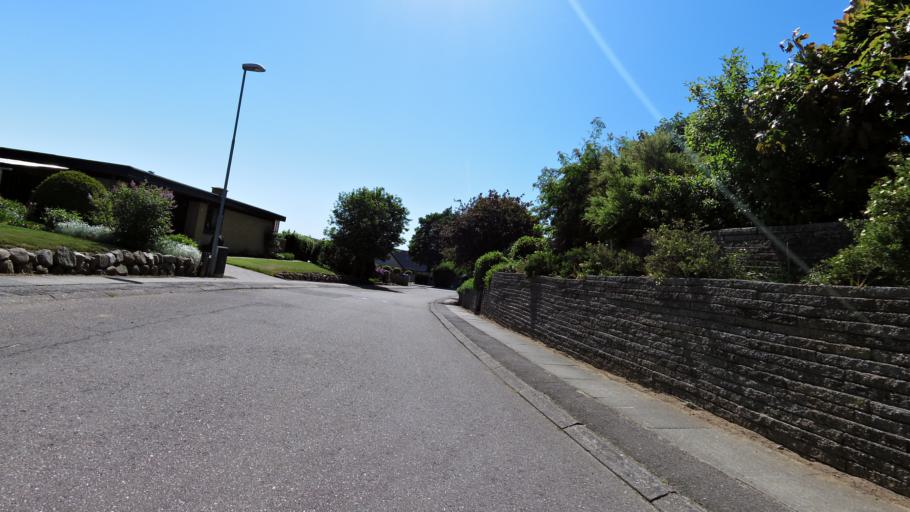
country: DK
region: Central Jutland
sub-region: Arhus Kommune
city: Framlev
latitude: 56.1436
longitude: 9.9968
